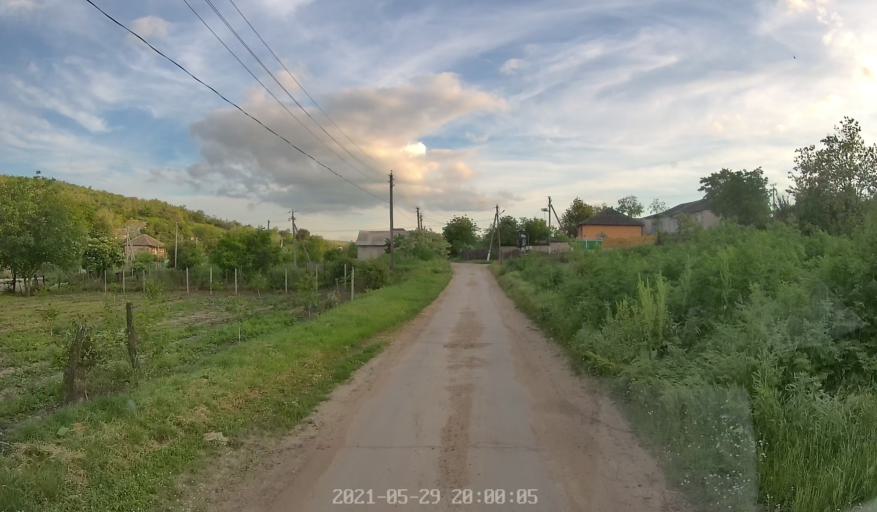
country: MD
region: Chisinau
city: Singera
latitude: 46.8280
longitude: 28.9765
